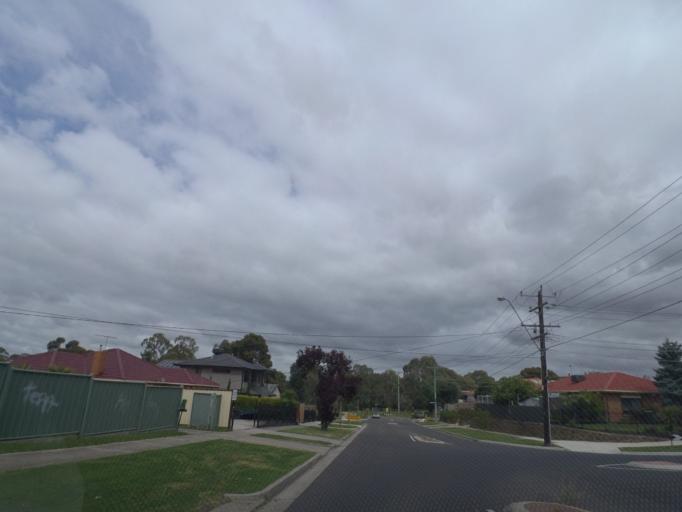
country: AU
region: Victoria
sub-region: Brimbank
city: Deer Park
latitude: -37.7598
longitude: 144.7657
